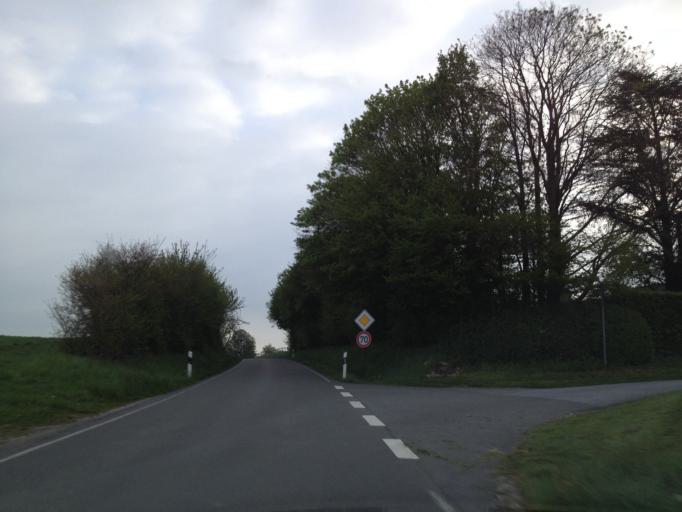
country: DE
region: North Rhine-Westphalia
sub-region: Regierungsbezirk Arnsberg
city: Anrochte
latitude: 51.5047
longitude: 8.2865
